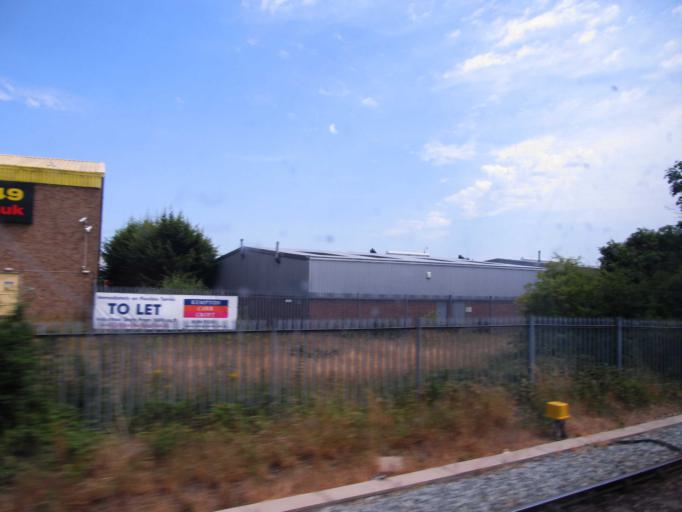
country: GB
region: England
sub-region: Slough
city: Slough
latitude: 51.5172
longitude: -0.6148
